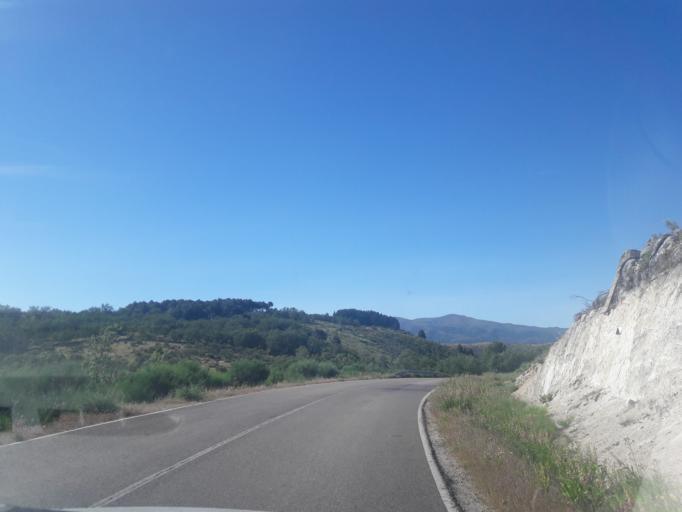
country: ES
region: Castille and Leon
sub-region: Provincia de Salamanca
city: Lagunilla
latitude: 40.3228
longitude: -5.9291
